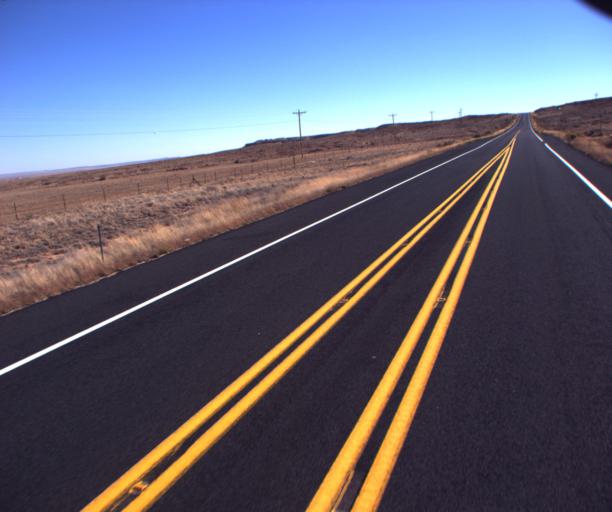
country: US
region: Arizona
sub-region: Coconino County
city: Tuba City
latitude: 35.9967
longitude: -111.0274
